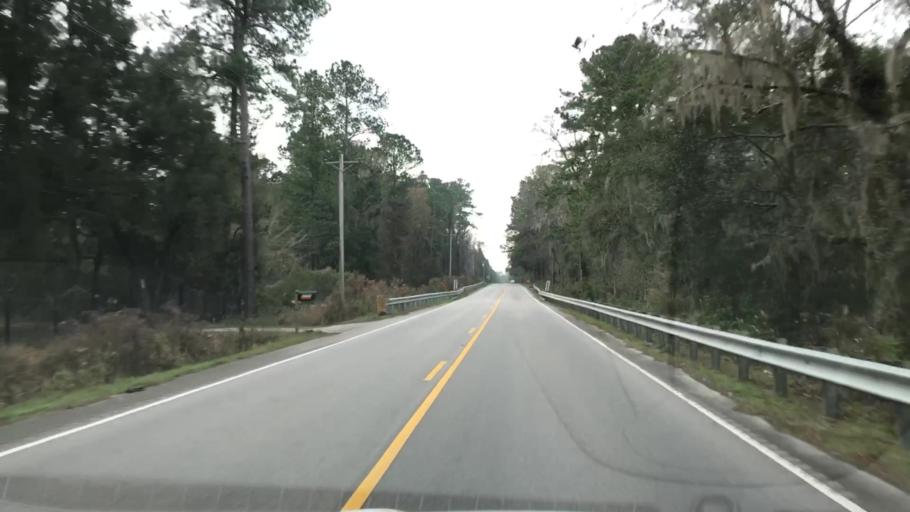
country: US
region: South Carolina
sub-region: Jasper County
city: Ridgeland
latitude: 32.5088
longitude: -80.8879
